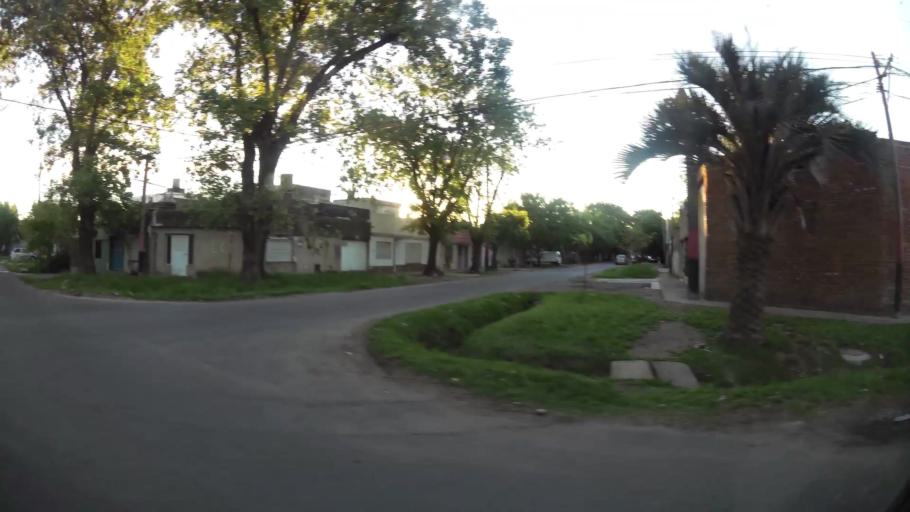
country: AR
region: Santa Fe
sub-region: Departamento de Rosario
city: Rosario
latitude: -32.9644
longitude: -60.6813
